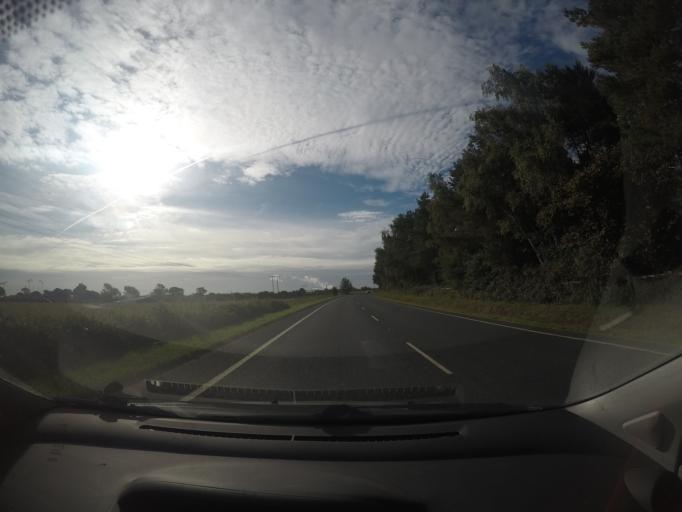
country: GB
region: England
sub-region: North Yorkshire
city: Barlby
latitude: 53.8068
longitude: -1.0369
